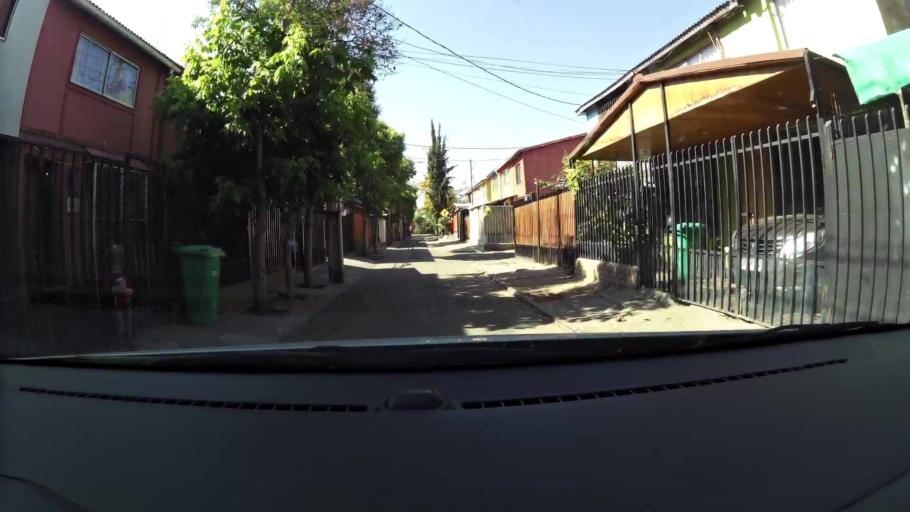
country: CL
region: Santiago Metropolitan
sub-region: Provincia de Maipo
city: San Bernardo
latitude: -33.5642
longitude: -70.7029
